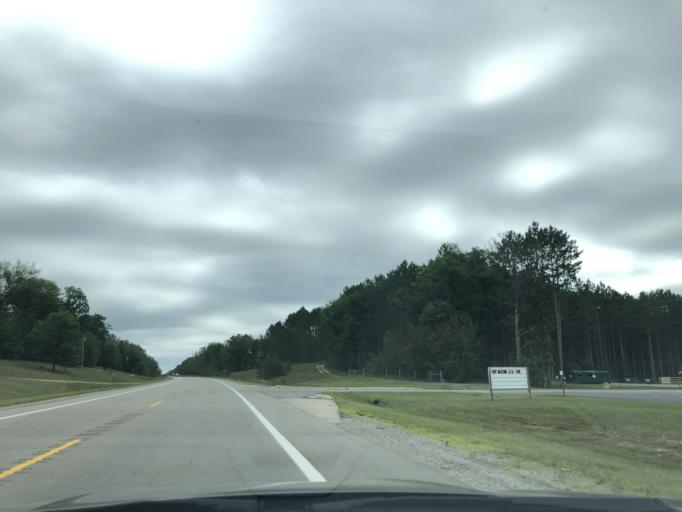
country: US
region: Michigan
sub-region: Clare County
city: Harrison
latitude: 44.0315
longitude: -85.0168
